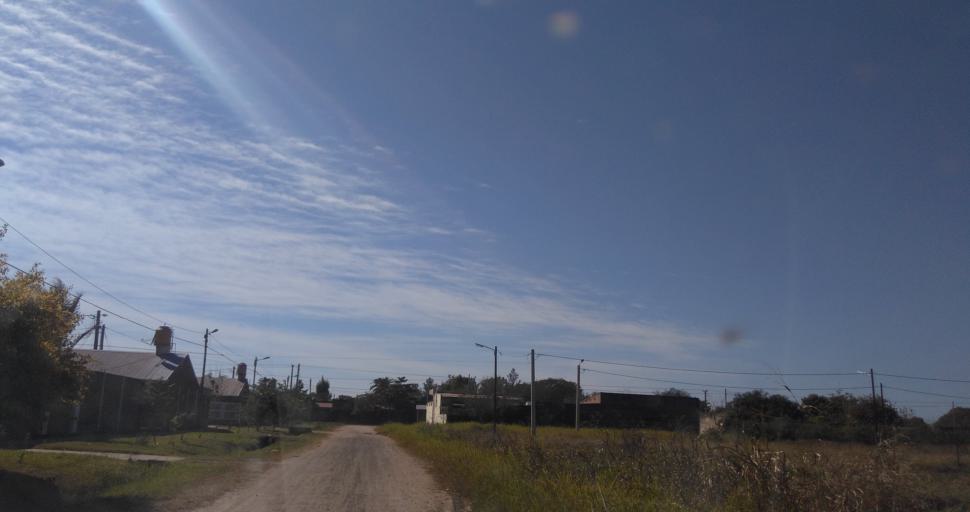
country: AR
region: Chaco
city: Fontana
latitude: -27.4498
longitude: -59.0331
